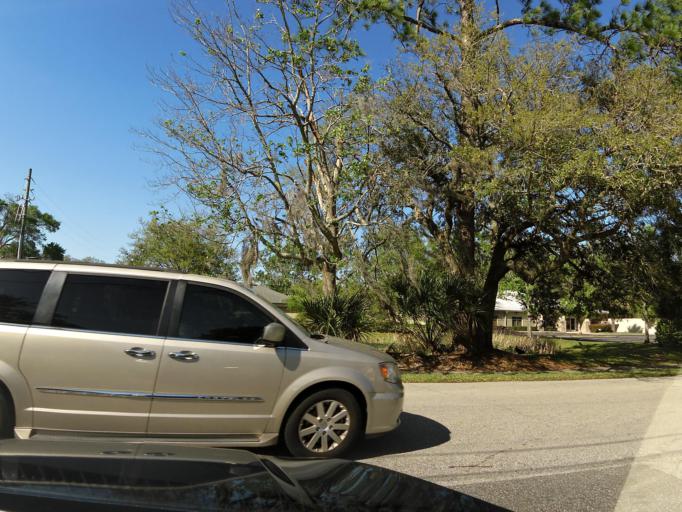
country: US
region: Florida
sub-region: Duval County
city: Jacksonville
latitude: 30.2809
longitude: -81.6004
